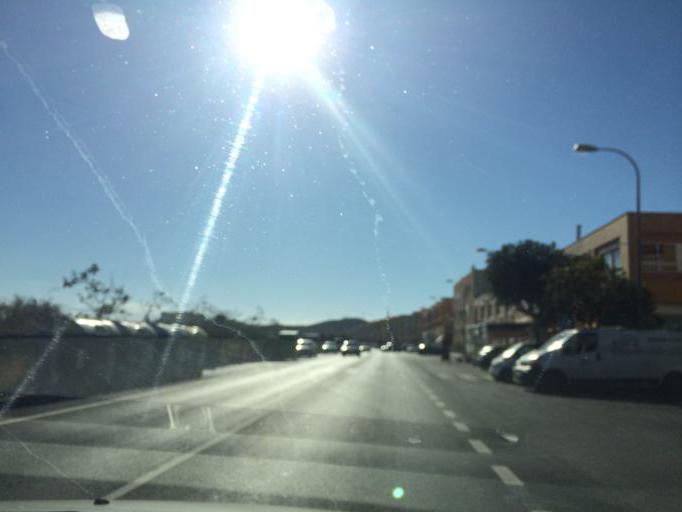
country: ES
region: Andalusia
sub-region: Provincia de Almeria
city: Huercal de Almeria
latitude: 36.8774
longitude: -2.4390
